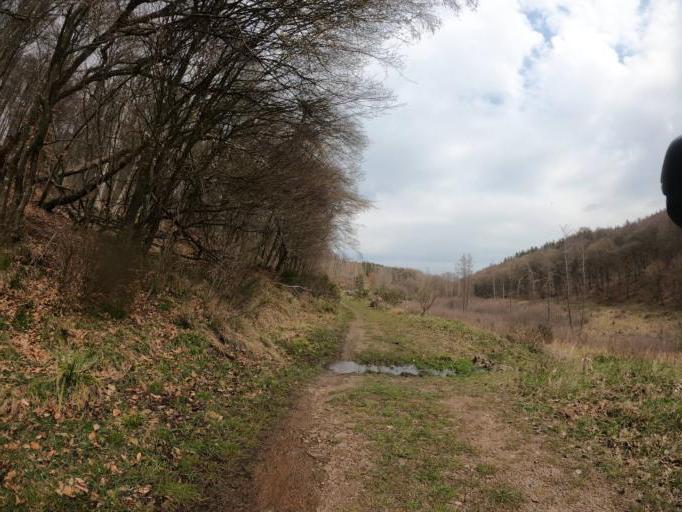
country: DE
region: North Rhine-Westphalia
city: Heimbach
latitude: 50.5961
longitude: 6.4680
